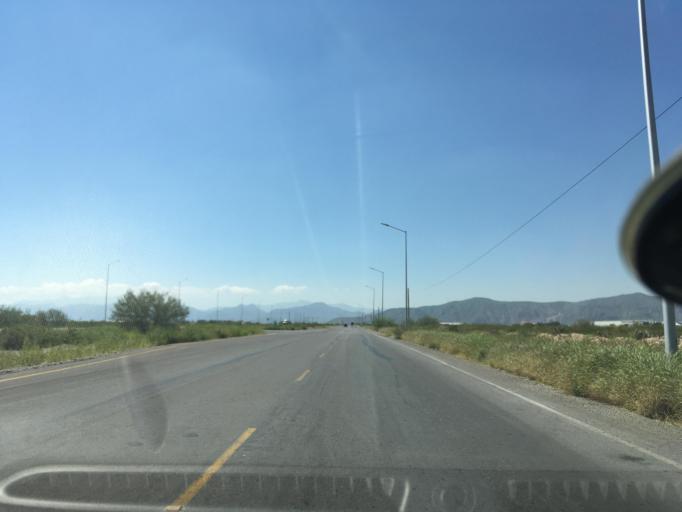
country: MX
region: Coahuila
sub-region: Torreon
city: Fraccionamiento la Noria
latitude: 25.4770
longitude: -103.3210
